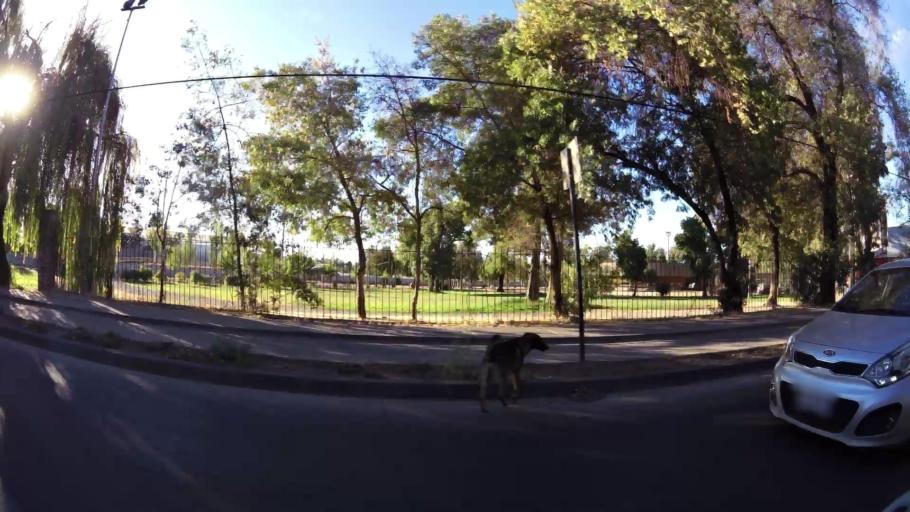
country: CL
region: Maule
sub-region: Provincia de Curico
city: Curico
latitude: -34.9749
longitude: -71.2281
